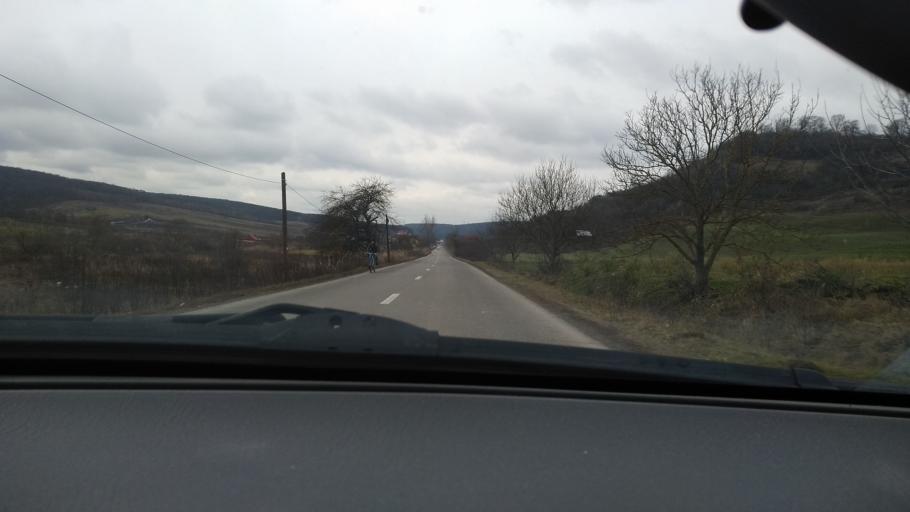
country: RO
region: Mures
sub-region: Comuna Livezeni
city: Livezeni
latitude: 46.5446
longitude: 24.6555
